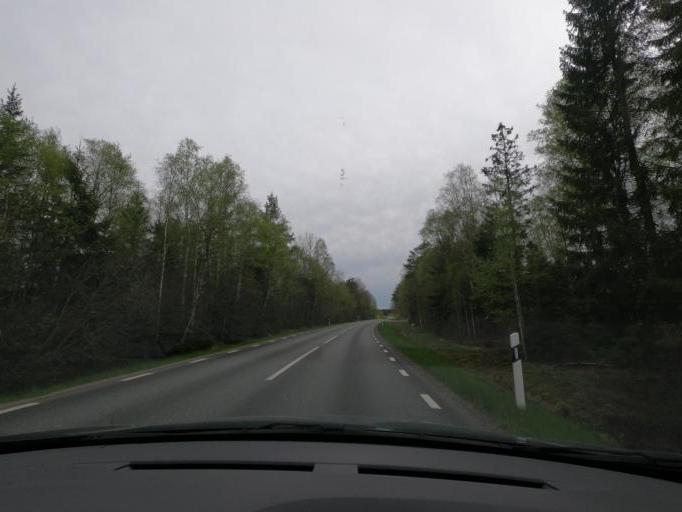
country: SE
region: Joenkoeping
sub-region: Varnamo Kommun
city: Bredaryd
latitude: 57.2071
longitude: 13.7654
